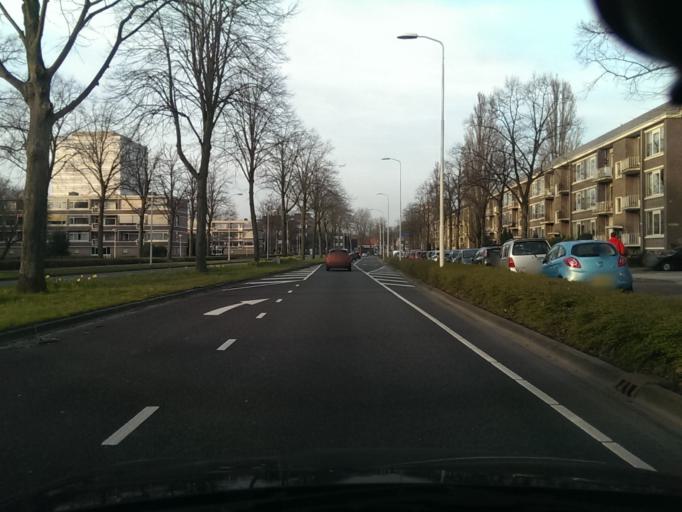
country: NL
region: North Brabant
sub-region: Gemeente Eindhoven
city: Eindhoven
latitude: 51.4309
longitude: 5.4632
